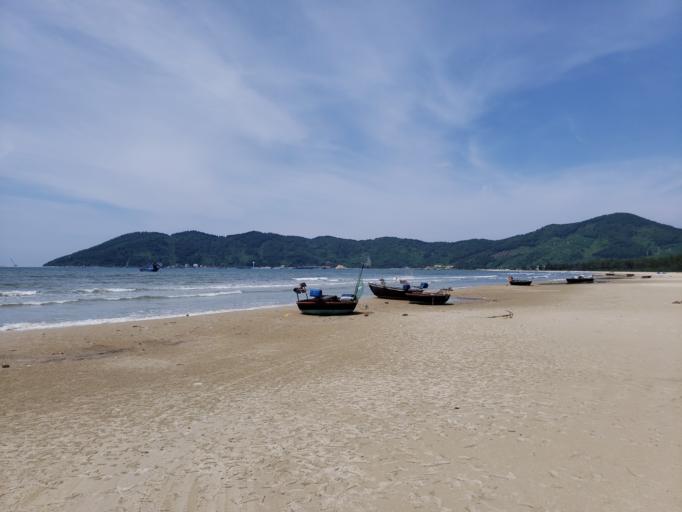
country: VN
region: Thua Thien-Hue
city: Phu Loc
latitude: 16.3130
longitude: 108.0040
